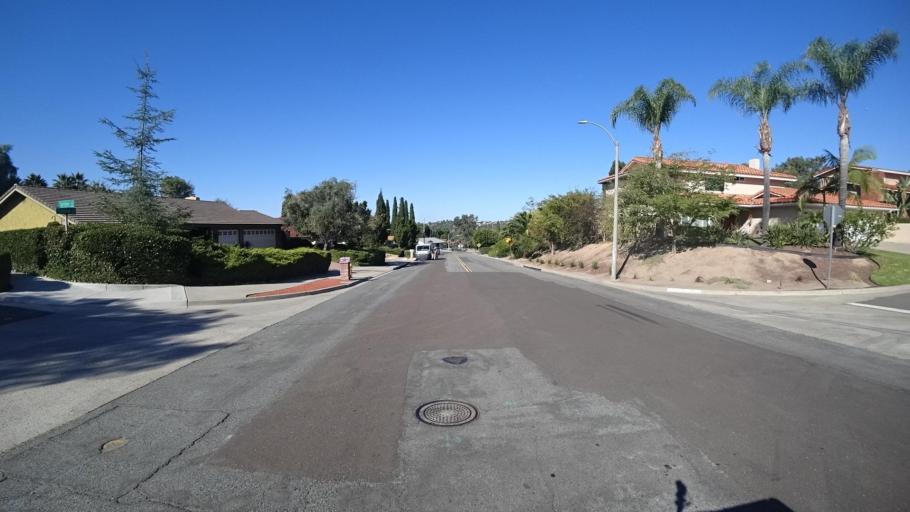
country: US
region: California
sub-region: San Diego County
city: Bonita
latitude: 32.6718
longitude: -117.0073
